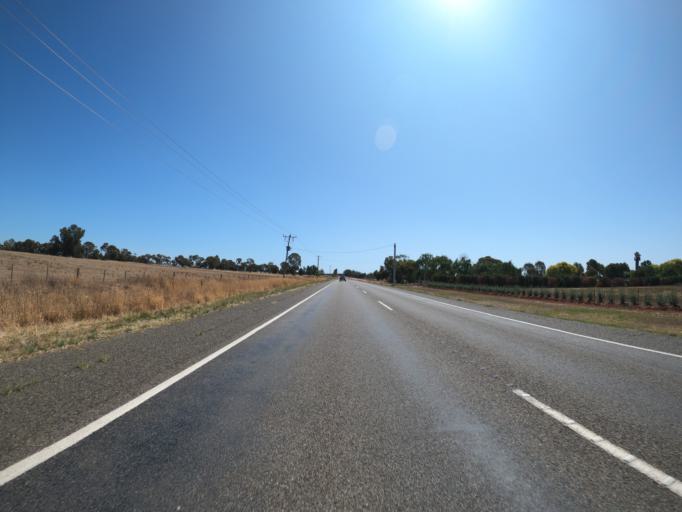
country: AU
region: Victoria
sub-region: Moira
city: Yarrawonga
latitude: -36.0266
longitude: 146.0864
